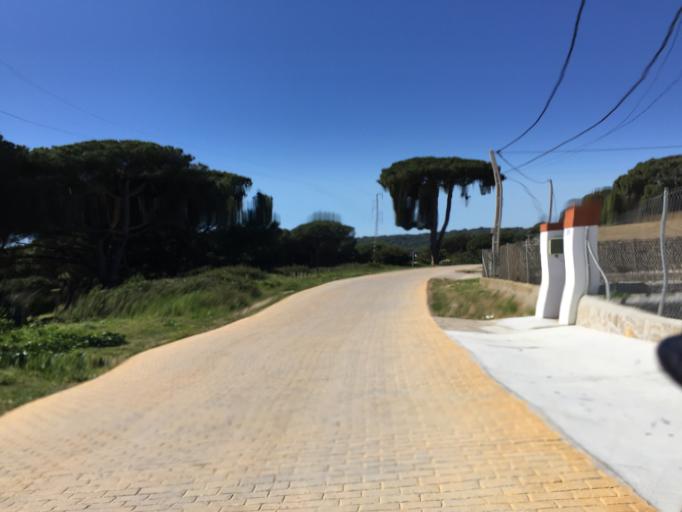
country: ES
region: Andalusia
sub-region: Provincia de Cadiz
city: Vejer de la Frontera
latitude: 36.2058
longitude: -5.9827
